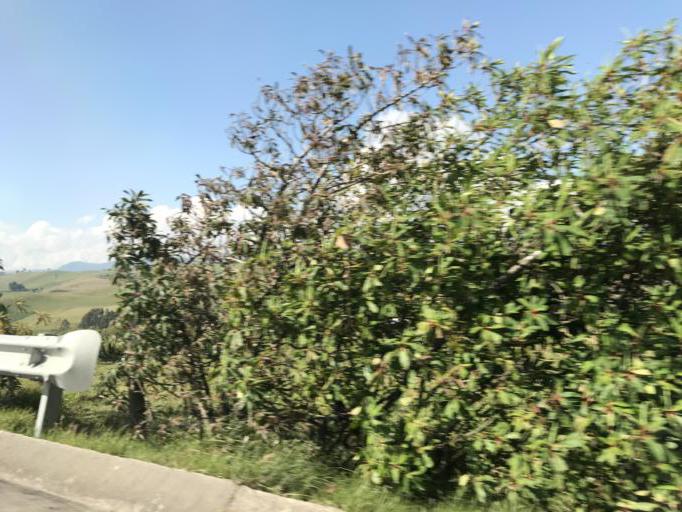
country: CO
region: Cauca
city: Paispamba
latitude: 2.2617
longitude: -76.5071
